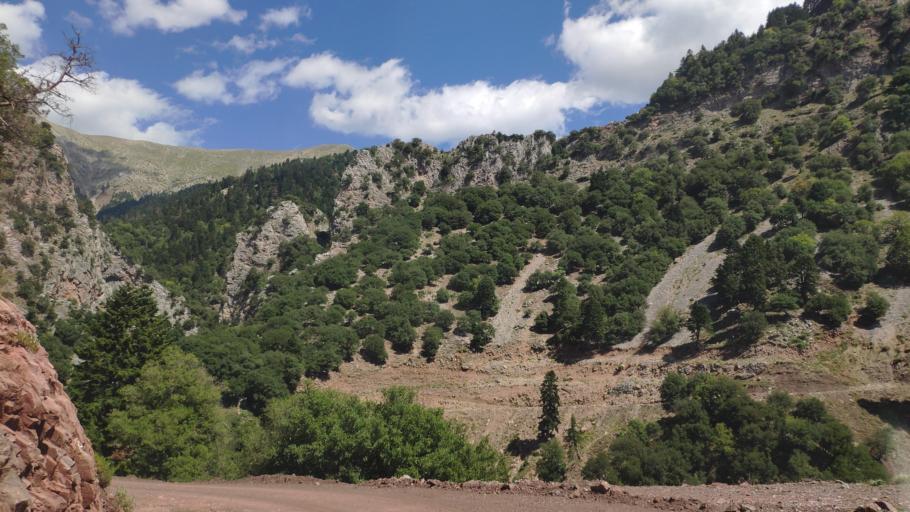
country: GR
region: Central Greece
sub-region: Nomos Evrytanias
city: Kerasochori
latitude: 39.1399
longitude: 21.6565
